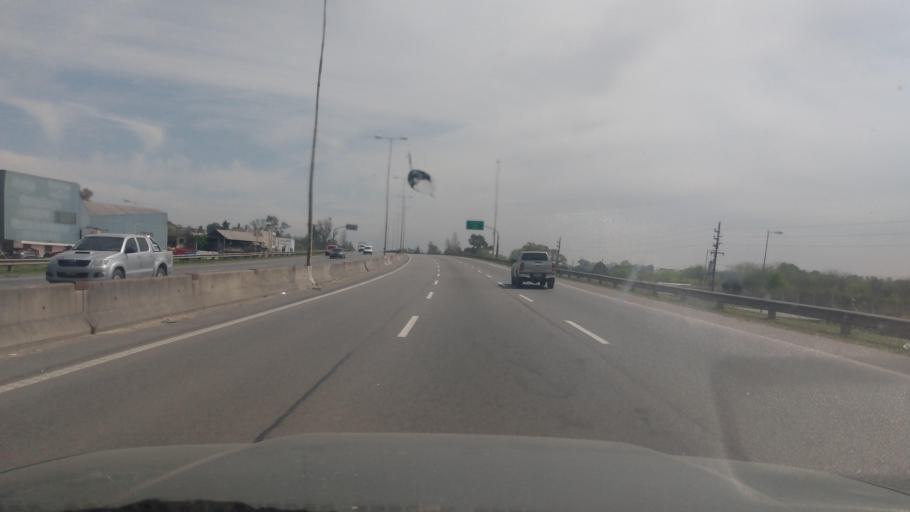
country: AR
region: Buenos Aires
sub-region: Partido de Pilar
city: Pilar
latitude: -34.4410
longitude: -58.9666
